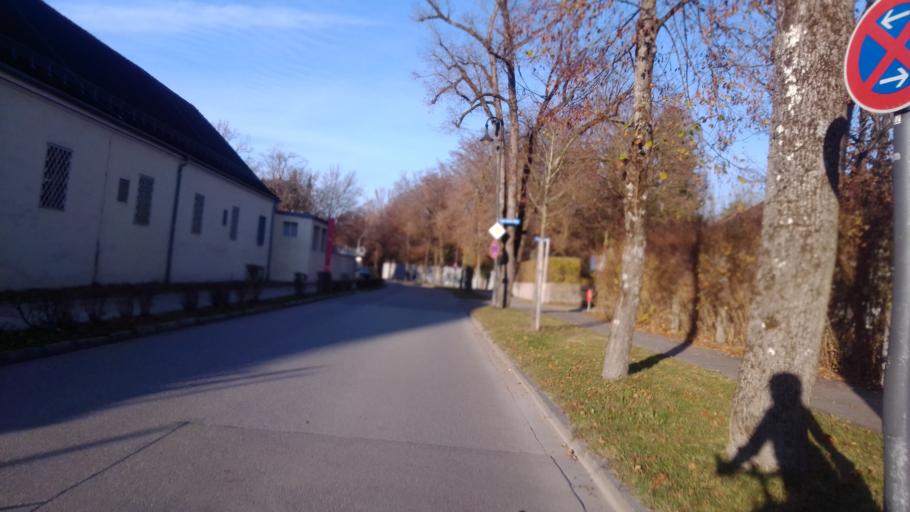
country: DE
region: Bavaria
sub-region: Upper Bavaria
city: Pullach im Isartal
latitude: 48.0605
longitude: 11.5274
